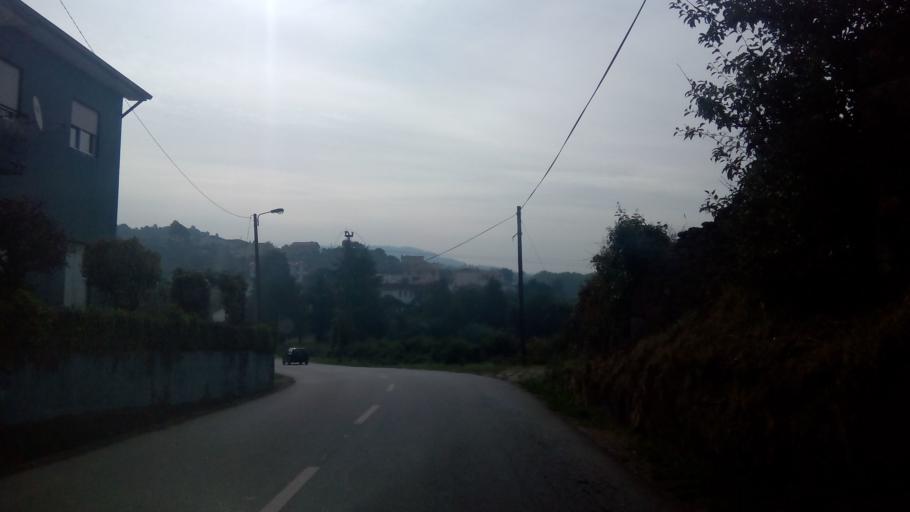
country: PT
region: Porto
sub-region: Paredes
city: Gandra
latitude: 41.1942
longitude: -8.4325
